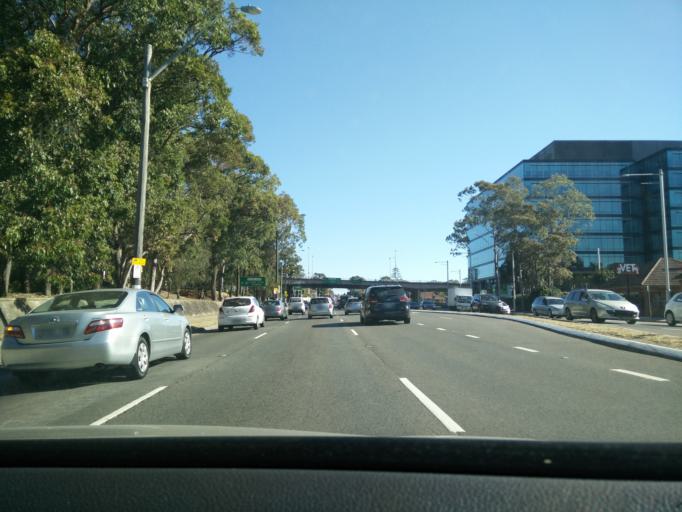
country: AU
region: New South Wales
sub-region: Ryde
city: North Ryde
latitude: -33.7863
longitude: 151.1273
